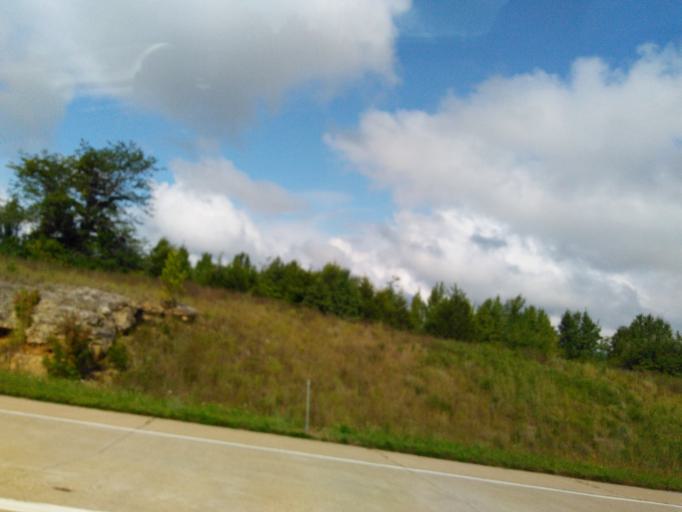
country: US
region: Missouri
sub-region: Jefferson County
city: Hillsboro
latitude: 38.2630
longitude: -90.5534
